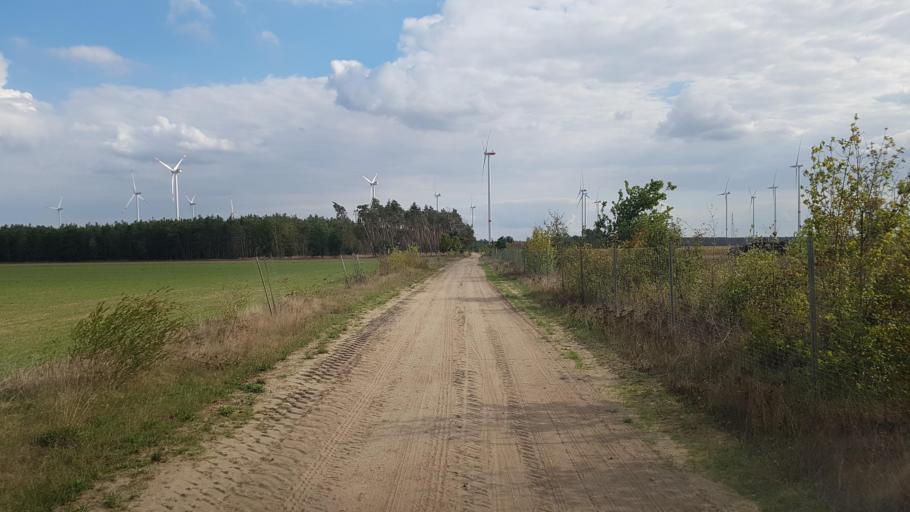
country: DE
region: Saxony
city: Arzberg
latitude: 51.5784
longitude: 13.1751
